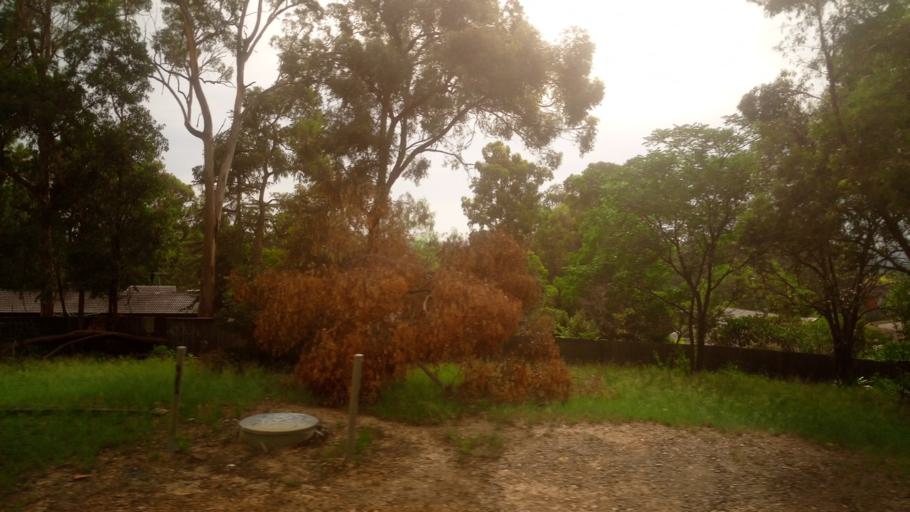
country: AU
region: New South Wales
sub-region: Blue Mountains Municipality
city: Glenbrook
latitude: -33.7645
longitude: 150.6418
